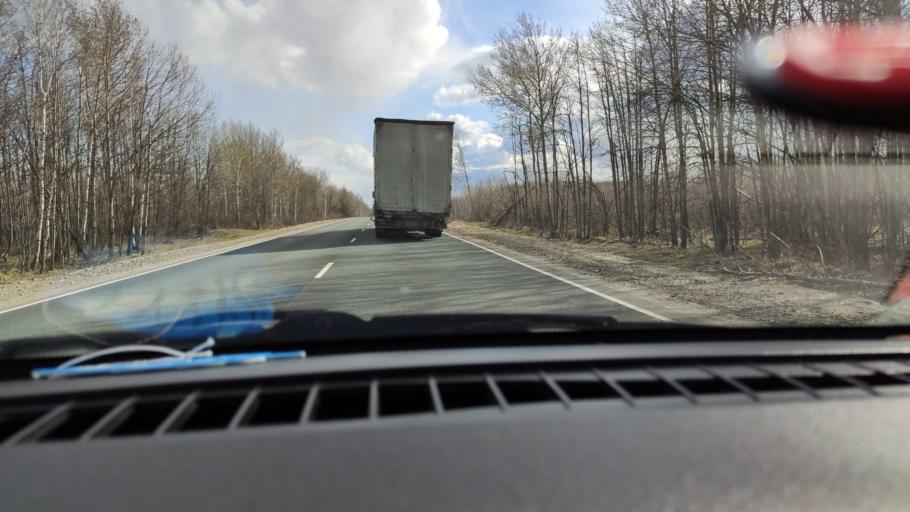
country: RU
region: Saratov
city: Khvalynsk
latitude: 52.4249
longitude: 48.0084
